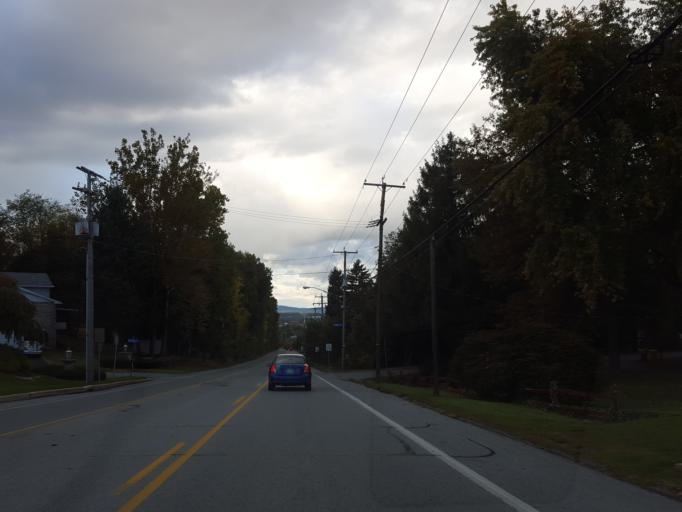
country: US
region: Pennsylvania
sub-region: York County
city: Valley View
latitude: 39.9443
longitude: -76.7070
